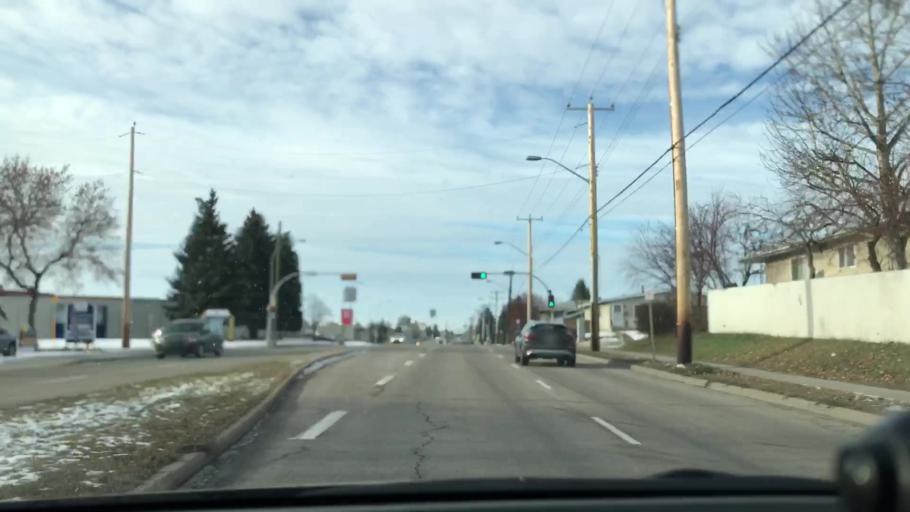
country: CA
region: Alberta
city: Edmonton
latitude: 53.4883
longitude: -113.5071
